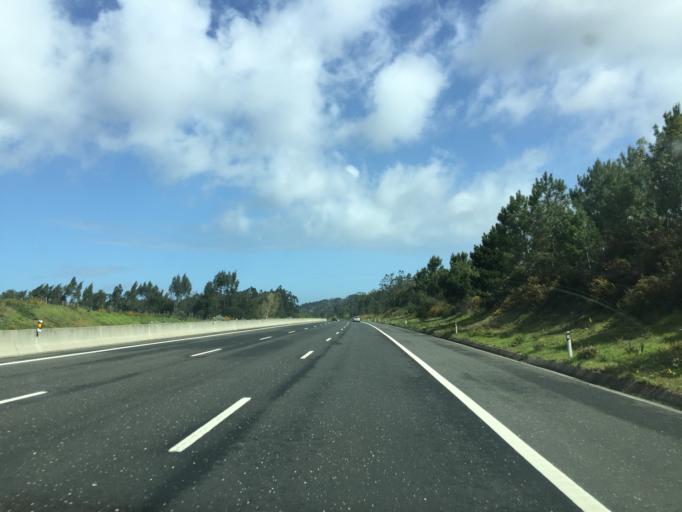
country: PT
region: Leiria
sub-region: Caldas da Rainha
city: Caldas da Rainha
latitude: 39.4718
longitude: -9.1070
